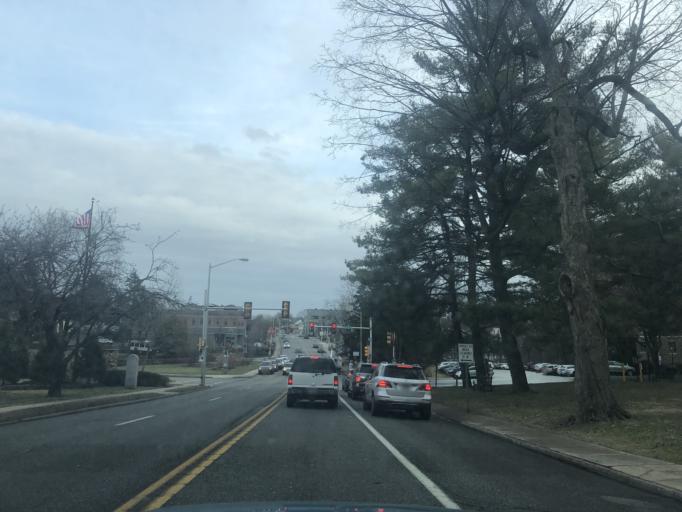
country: US
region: Pennsylvania
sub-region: Montgomery County
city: Bryn Mawr
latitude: 40.0276
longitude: -75.3303
